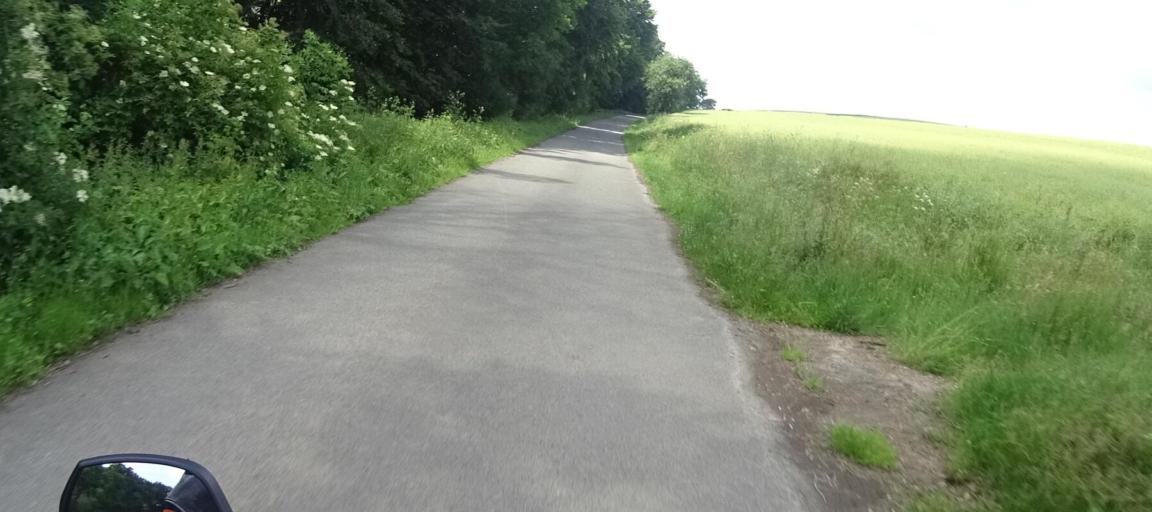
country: DE
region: Lower Saxony
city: Polle
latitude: 51.9126
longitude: 9.3952
